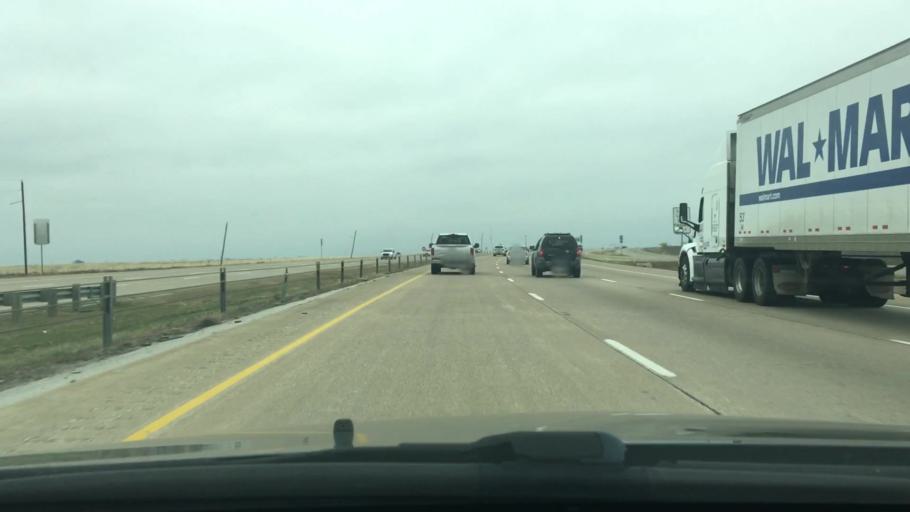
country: US
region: Texas
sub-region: Ellis County
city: Ennis
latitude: 32.2702
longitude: -96.5114
